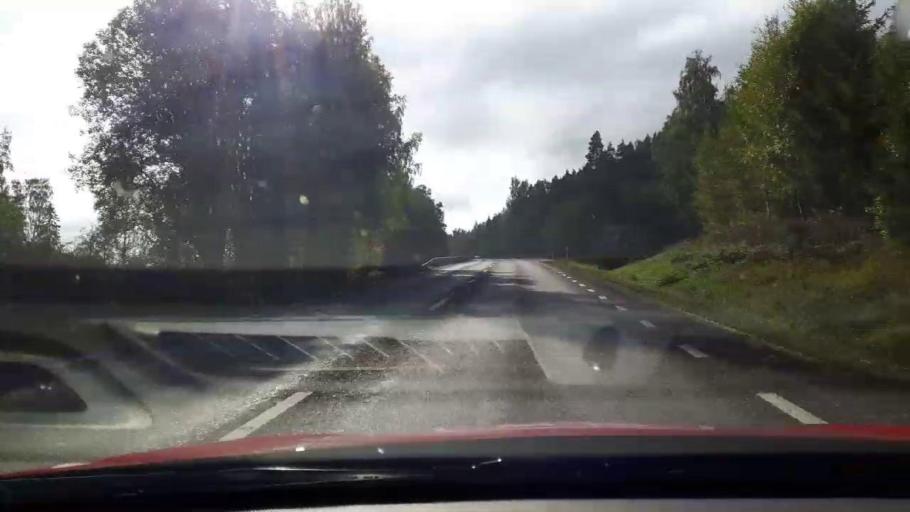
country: SE
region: Gaevleborg
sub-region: Ljusdals Kommun
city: Jaervsoe
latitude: 61.7434
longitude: 16.1587
